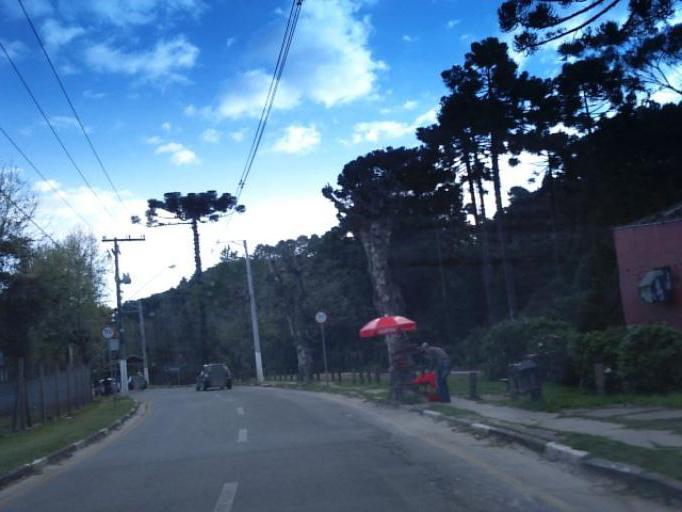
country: BR
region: Sao Paulo
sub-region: Campos Do Jordao
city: Campos do Jordao
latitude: -22.7202
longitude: -45.5737
